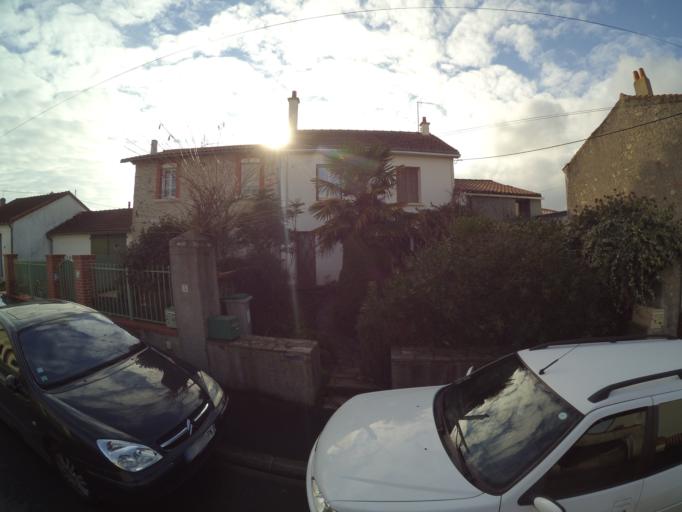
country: FR
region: Pays de la Loire
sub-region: Departement de la Loire-Atlantique
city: Clisson
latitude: 47.0810
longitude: -1.2769
